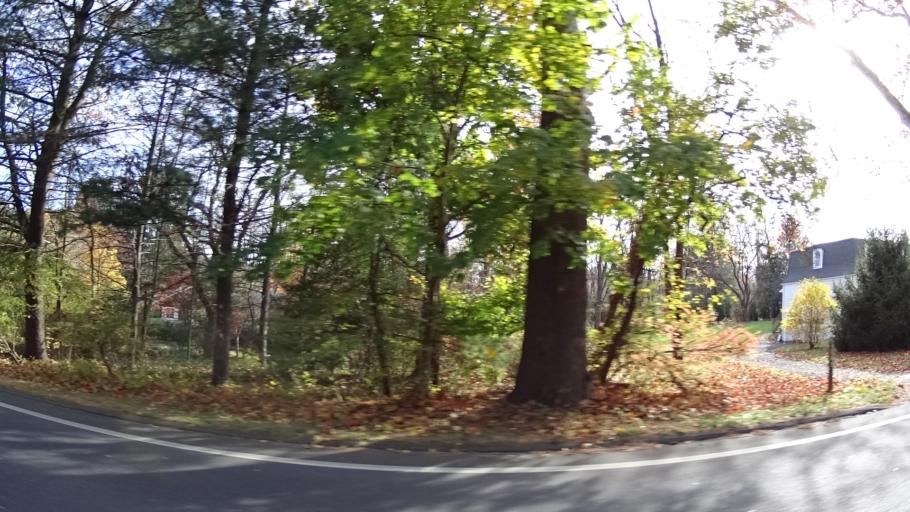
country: US
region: New Jersey
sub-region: Morris County
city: Mendham
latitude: 40.7874
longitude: -74.5643
